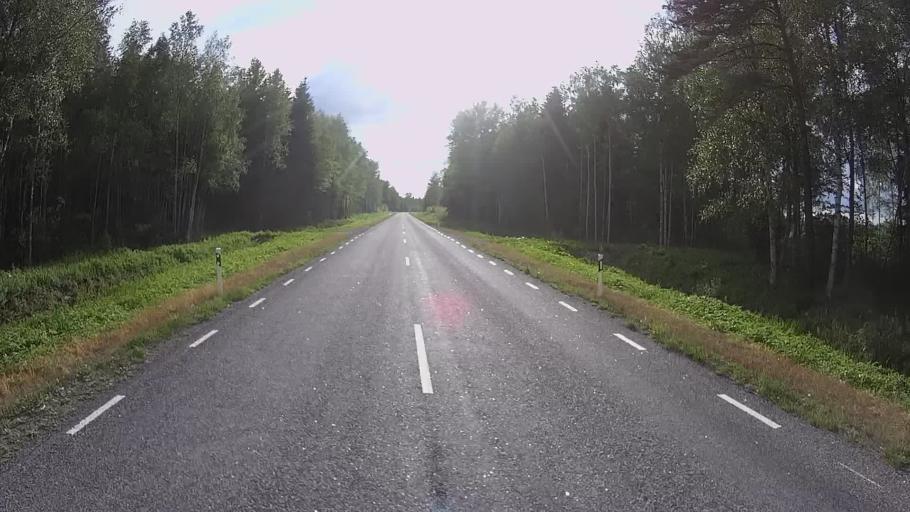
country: EE
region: Jogevamaa
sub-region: Mustvee linn
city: Mustvee
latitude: 59.0223
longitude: 27.0573
